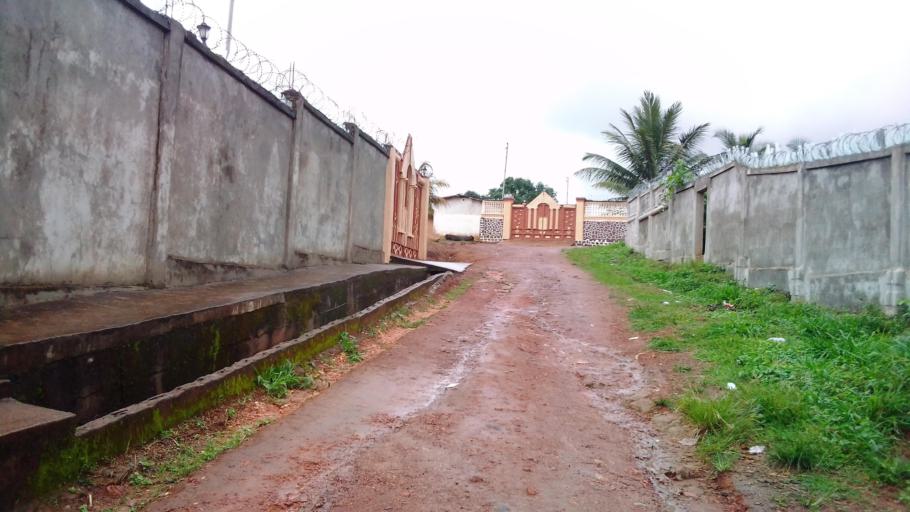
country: SL
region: Eastern Province
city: Kenema
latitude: 7.8752
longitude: -11.1777
